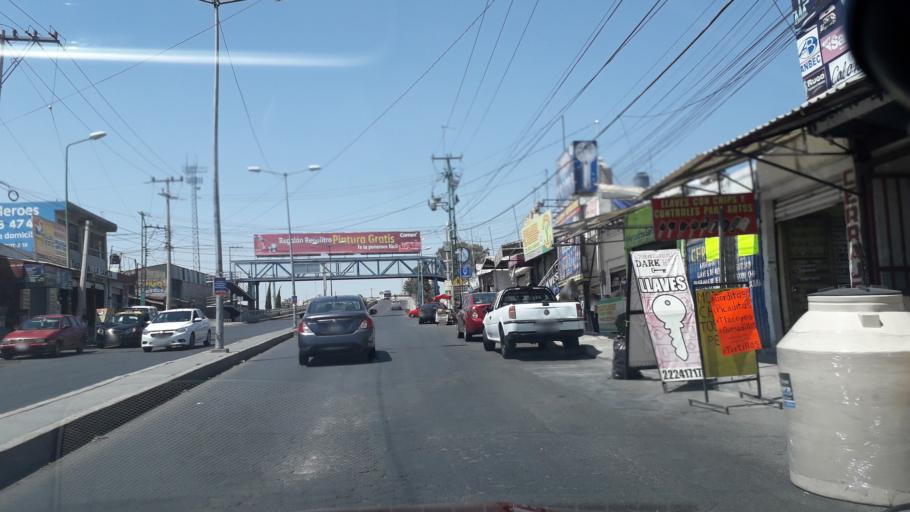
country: MX
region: Puebla
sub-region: Puebla
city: El Capulo (La Quebradora)
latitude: 18.9756
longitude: -98.2187
